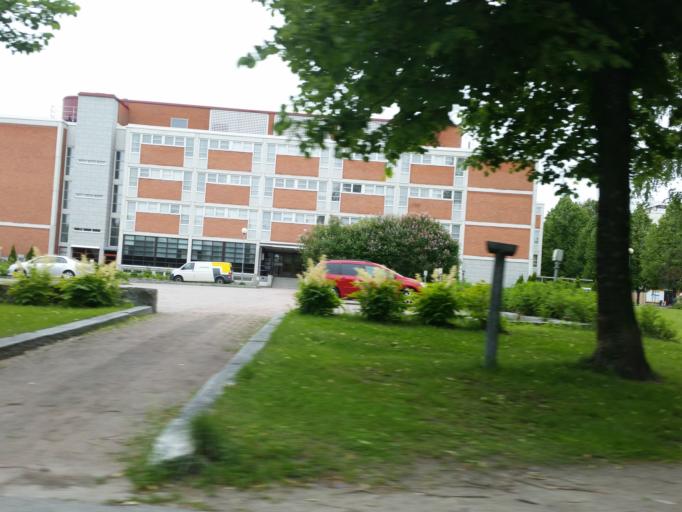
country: FI
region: Northern Savo
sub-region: Kuopio
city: Kuopio
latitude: 62.8885
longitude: 27.6807
